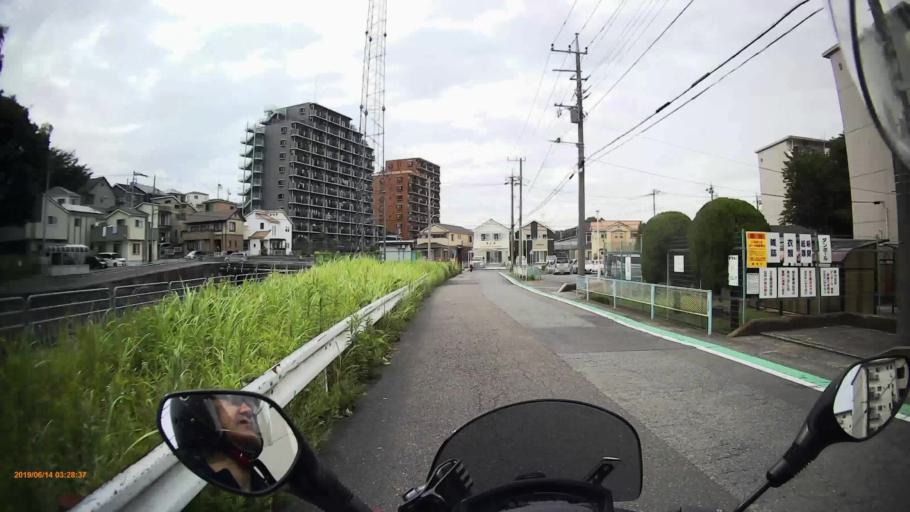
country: JP
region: Kanagawa
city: Minami-rinkan
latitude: 35.4147
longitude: 139.4481
